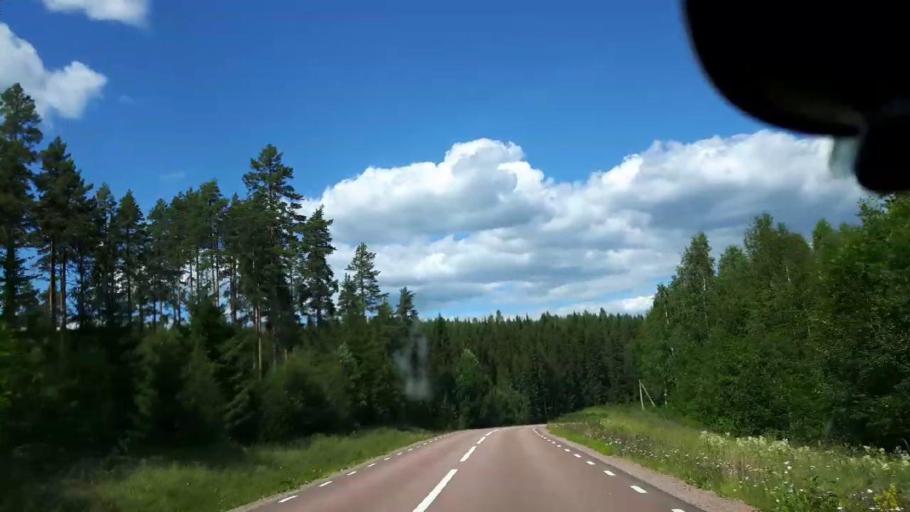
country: SE
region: Jaemtland
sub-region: Ragunda Kommun
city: Hammarstrand
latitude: 63.0346
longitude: 16.5174
